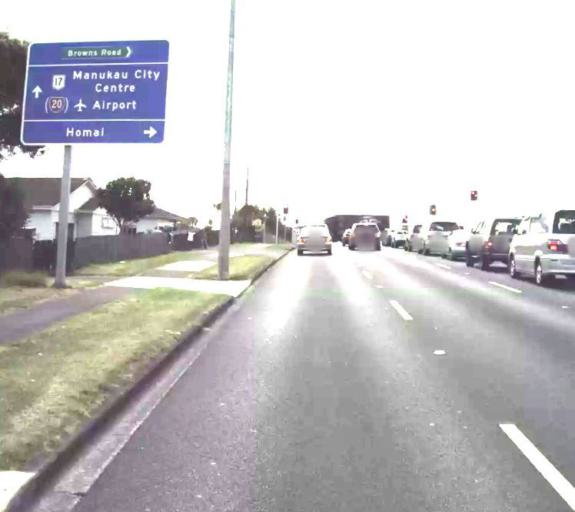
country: NZ
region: Auckland
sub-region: Auckland
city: Wiri
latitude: -37.0197
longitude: 174.8625
